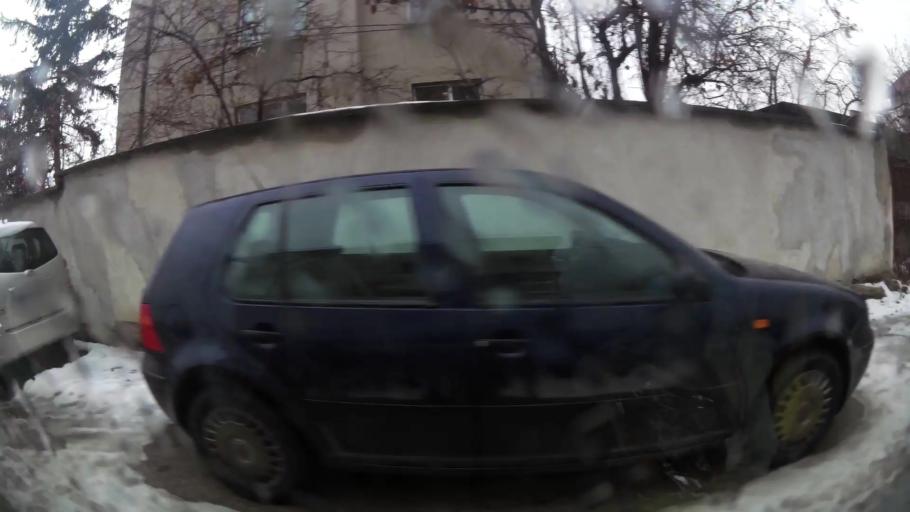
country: BG
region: Sofia-Capital
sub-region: Stolichna Obshtina
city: Sofia
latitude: 42.6821
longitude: 23.2667
